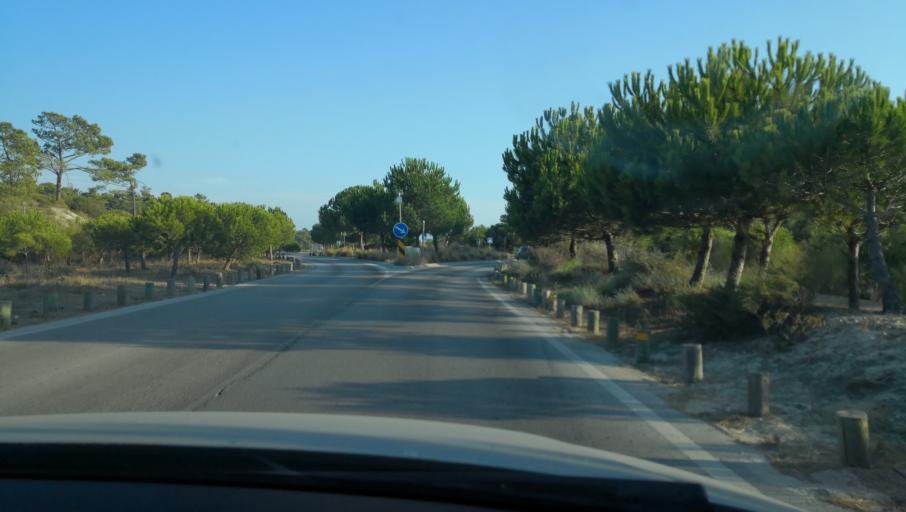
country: PT
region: Setubal
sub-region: Setubal
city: Setubal
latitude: 38.4763
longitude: -8.8872
